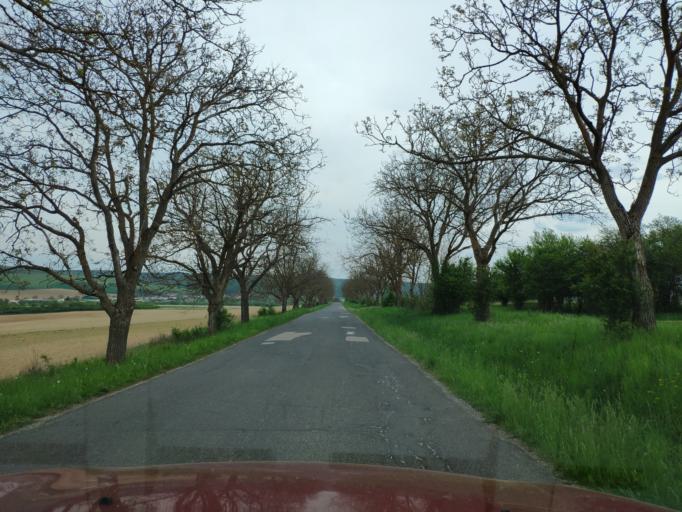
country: SK
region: Banskobystricky
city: Revuca
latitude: 48.4922
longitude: 20.2507
